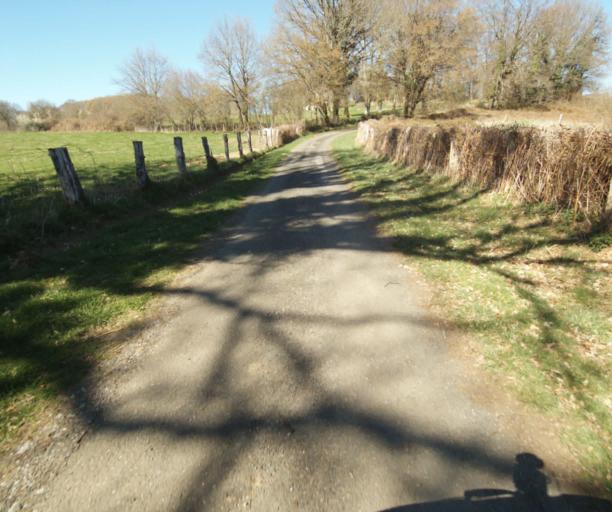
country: FR
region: Limousin
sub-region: Departement de la Correze
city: Chamboulive
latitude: 45.4056
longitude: 1.6413
